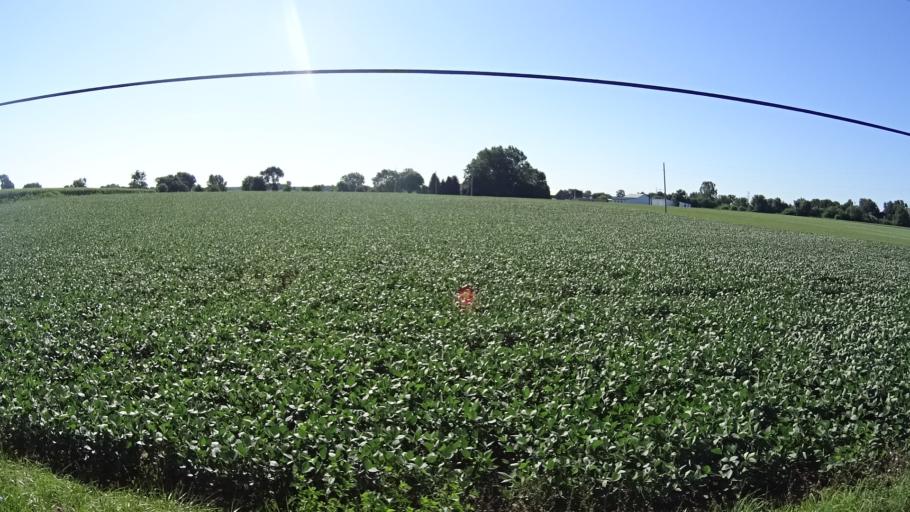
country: US
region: Ohio
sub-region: Erie County
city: Sandusky
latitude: 41.3949
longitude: -82.7535
